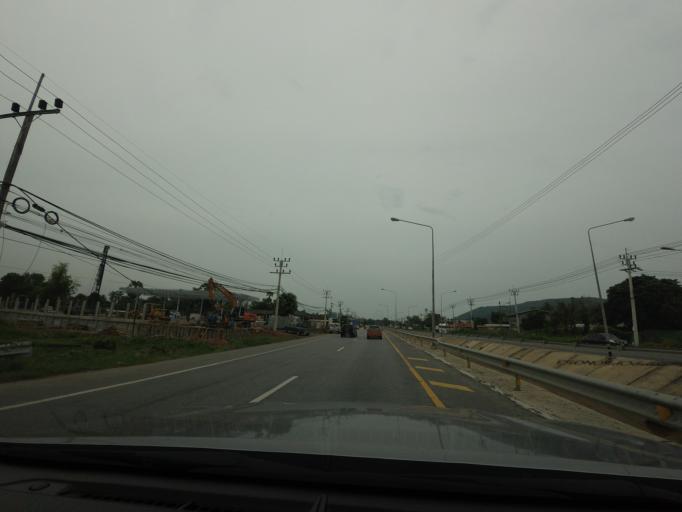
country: TH
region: Songkhla
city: Ban Mai
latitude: 7.2056
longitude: 100.5549
